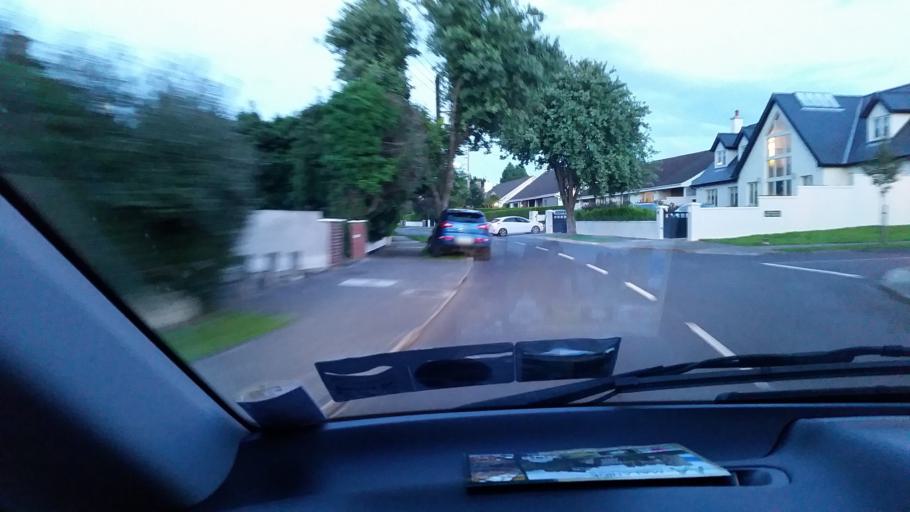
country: IE
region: Leinster
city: Foxrock
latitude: 53.2641
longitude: -6.1766
